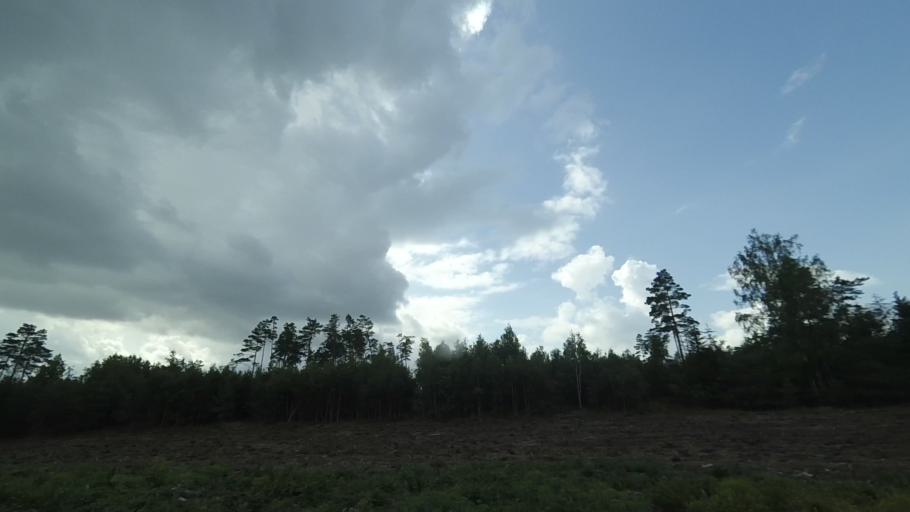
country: DK
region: Central Jutland
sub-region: Norddjurs Kommune
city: Allingabro
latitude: 56.4956
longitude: 10.3673
